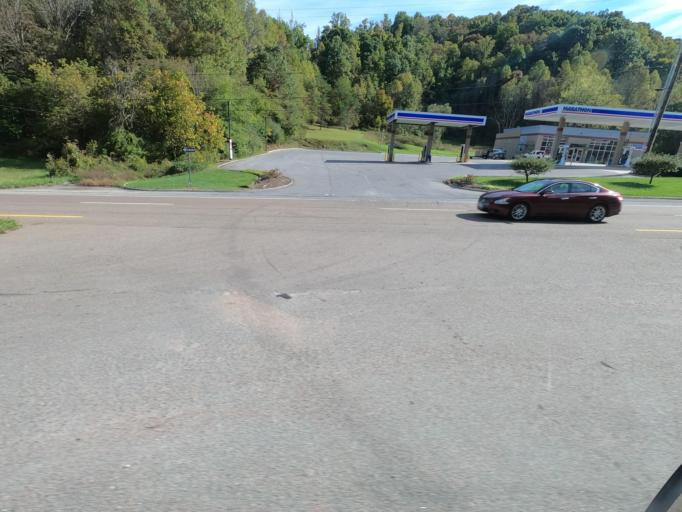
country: US
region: Tennessee
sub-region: Sullivan County
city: Walnut Hill
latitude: 36.5904
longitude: -82.2811
